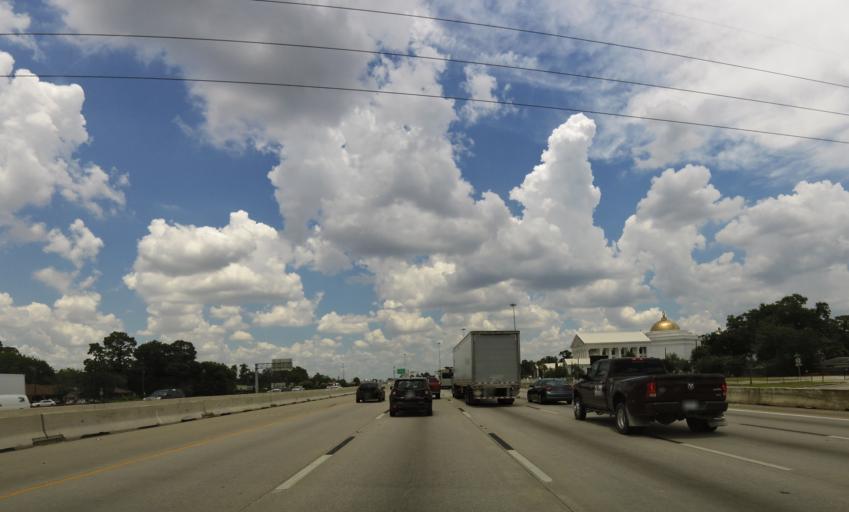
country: US
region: Texas
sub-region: Harris County
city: Houston
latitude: 29.8341
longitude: -95.3340
